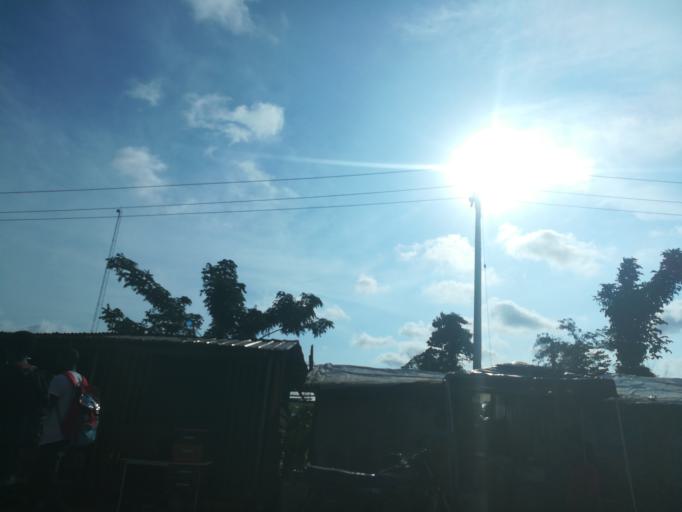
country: NG
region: Ogun
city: Ado Odo
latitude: 6.4980
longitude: 3.0850
